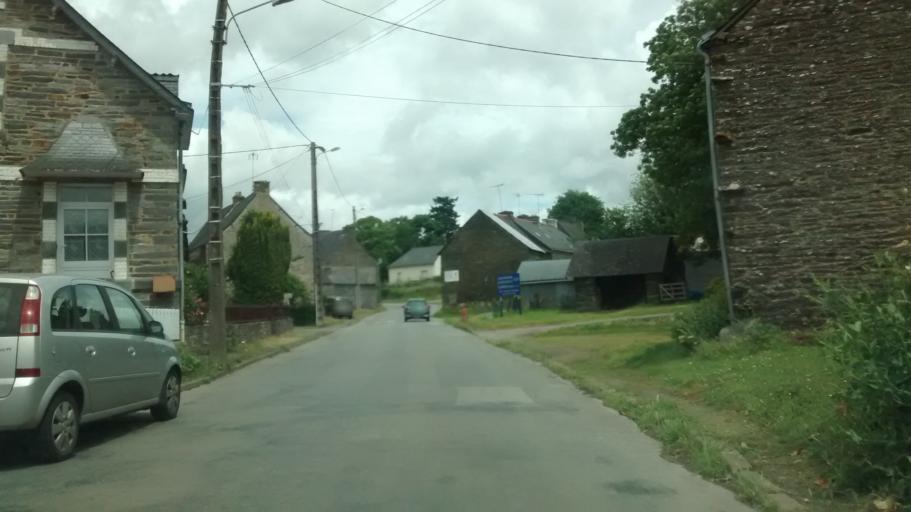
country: FR
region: Brittany
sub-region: Departement d'Ille-et-Vilaine
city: Sixt-sur-Aff
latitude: 47.7820
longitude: -2.1068
